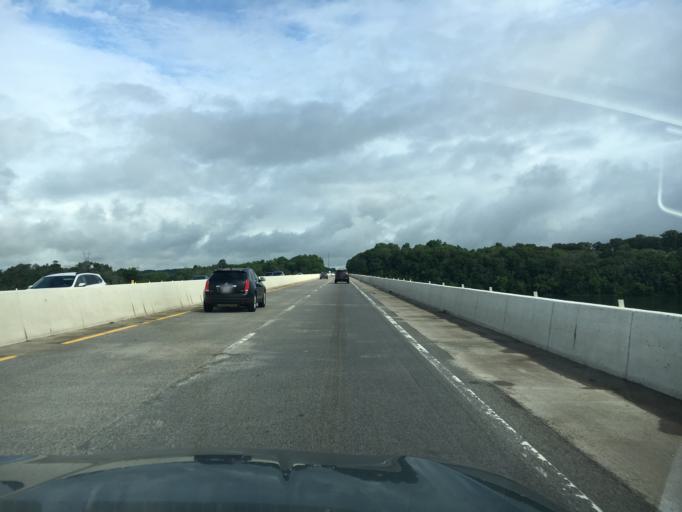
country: US
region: Tennessee
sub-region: Jefferson County
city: White Pine
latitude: 36.0396
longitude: -83.3330
